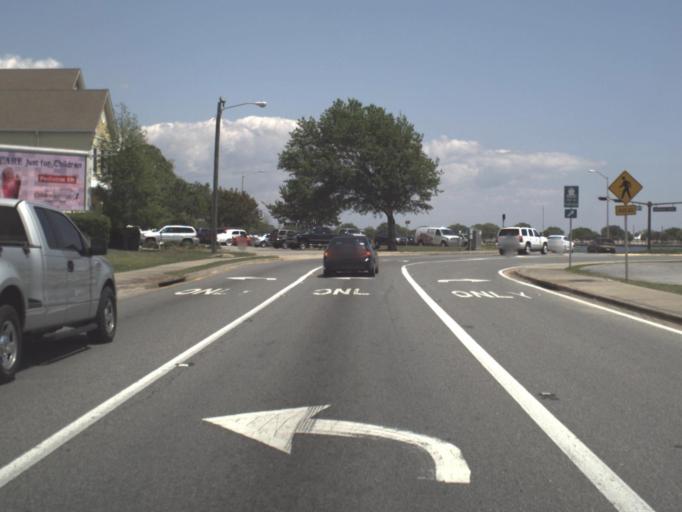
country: US
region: Florida
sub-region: Escambia County
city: Pensacola
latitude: 30.4168
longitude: -87.2007
